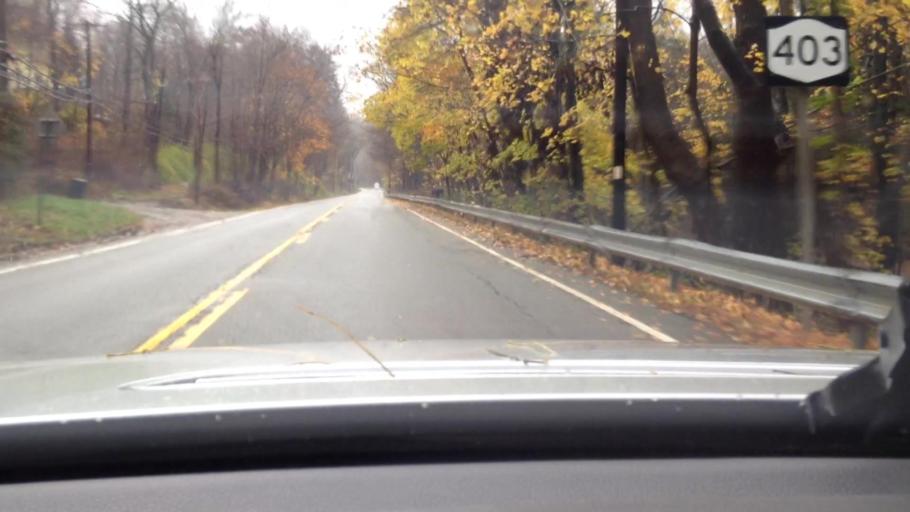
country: US
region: New York
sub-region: Orange County
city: West Point
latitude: 41.3677
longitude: -73.9295
